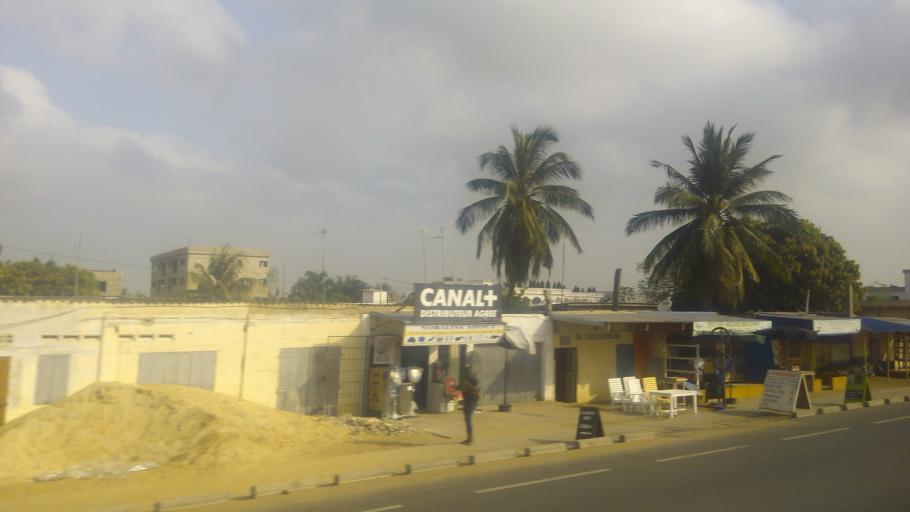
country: TG
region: Maritime
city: Lome
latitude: 6.1670
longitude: 1.3354
